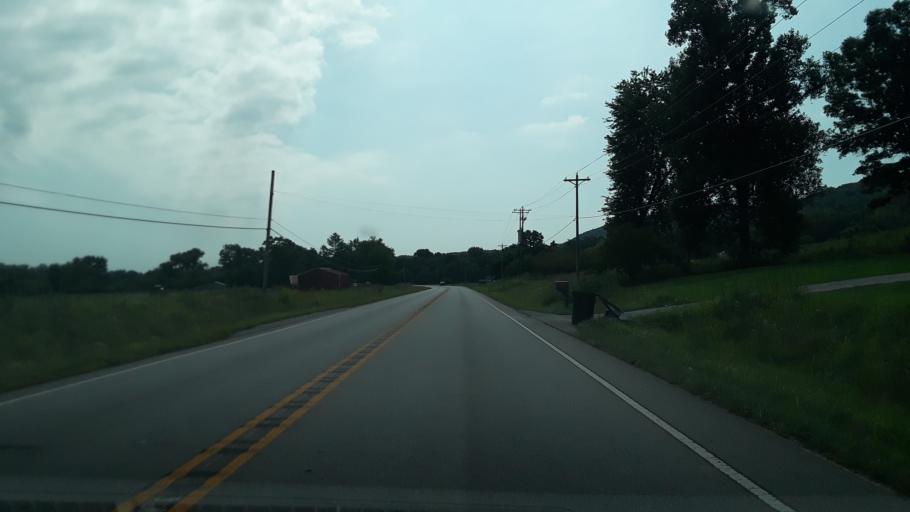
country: US
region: Indiana
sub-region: Clark County
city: Sellersburg
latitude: 38.4447
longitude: -85.8576
